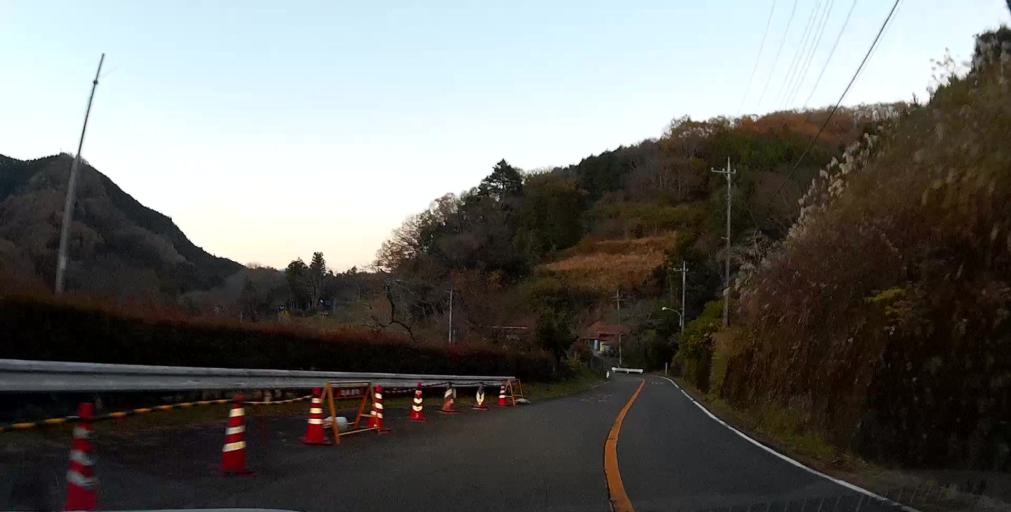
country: JP
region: Yamanashi
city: Uenohara
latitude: 35.5916
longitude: 139.1730
